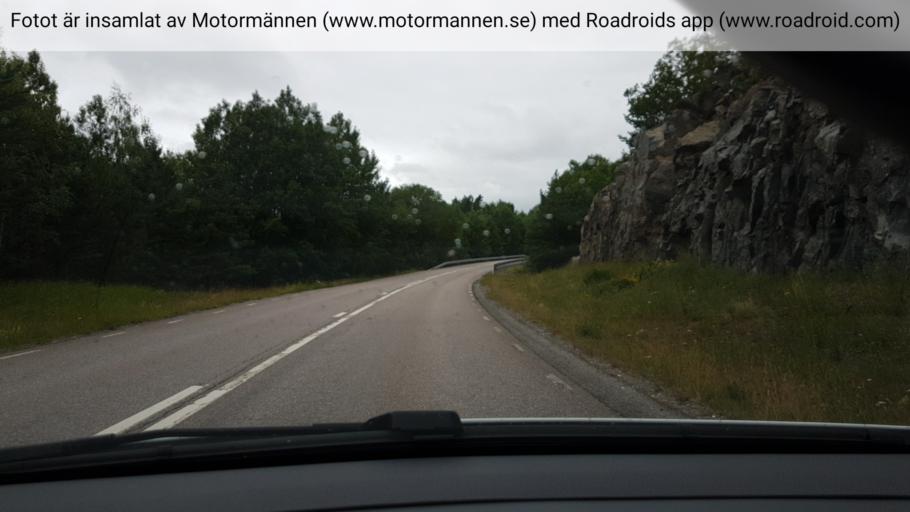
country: SE
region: Stockholm
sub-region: Vaxholms Kommun
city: Vaxholm
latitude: 59.3936
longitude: 18.4095
